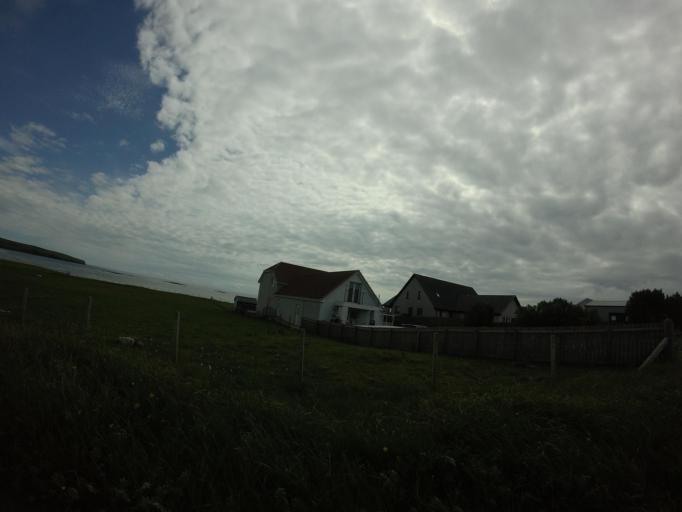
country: GB
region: Scotland
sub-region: Eilean Siar
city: Isle of Lewis
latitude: 58.2819
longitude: -6.2832
